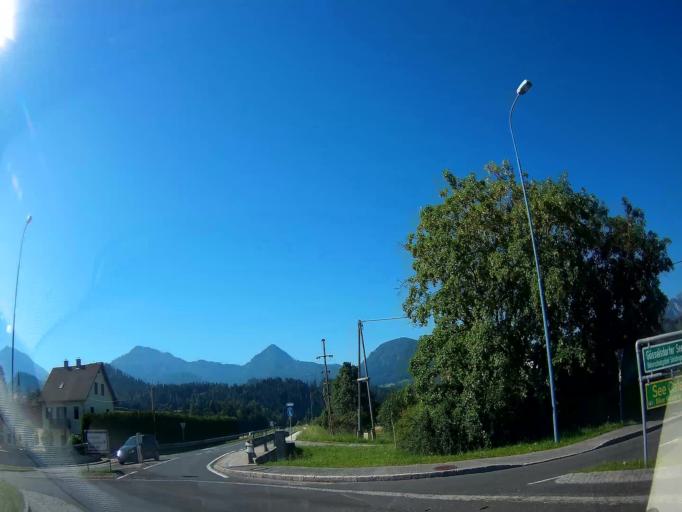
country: AT
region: Carinthia
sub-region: Politischer Bezirk Volkermarkt
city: Eberndorf
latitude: 46.5749
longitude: 14.6293
